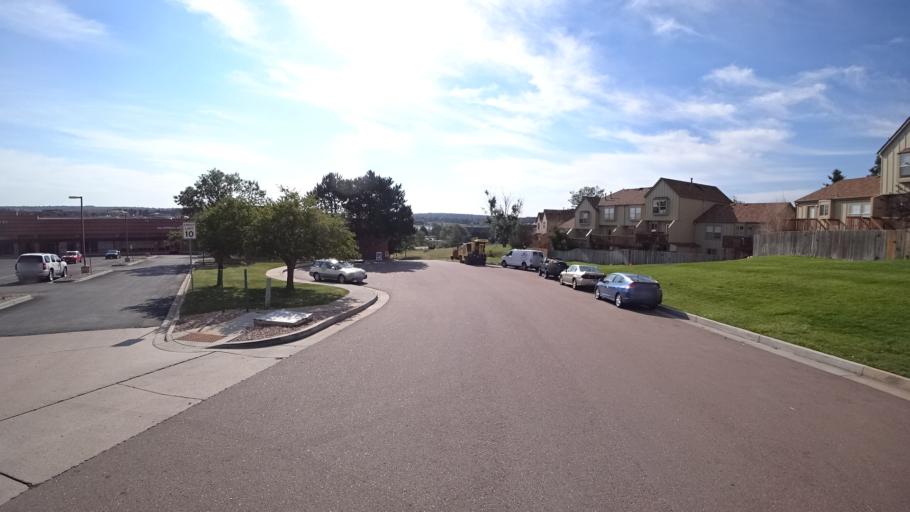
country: US
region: Colorado
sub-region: El Paso County
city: Air Force Academy
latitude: 38.9303
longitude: -104.8190
